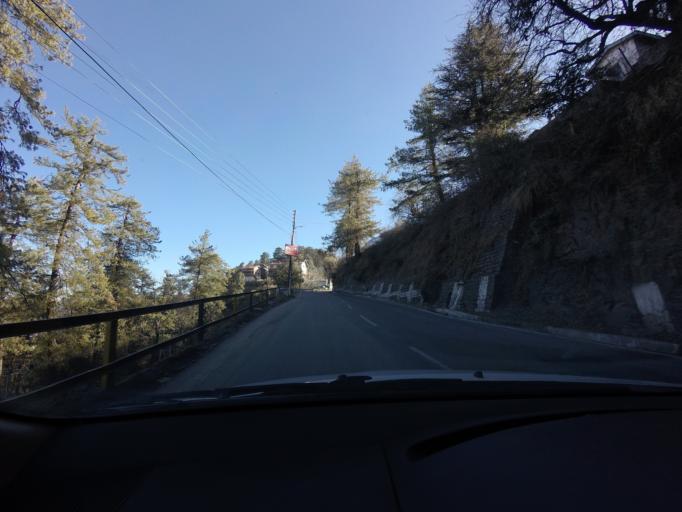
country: IN
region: Himachal Pradesh
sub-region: Shimla
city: Shimla
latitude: 31.1106
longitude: 77.2176
